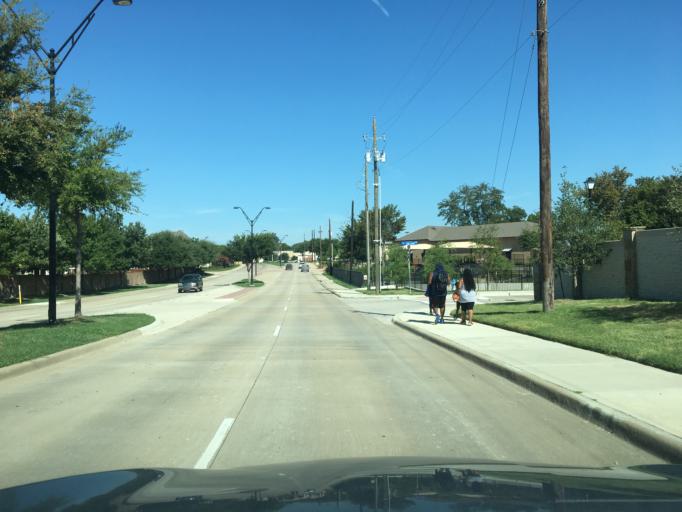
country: US
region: Texas
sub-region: Dallas County
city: Sachse
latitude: 32.9667
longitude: -96.6037
